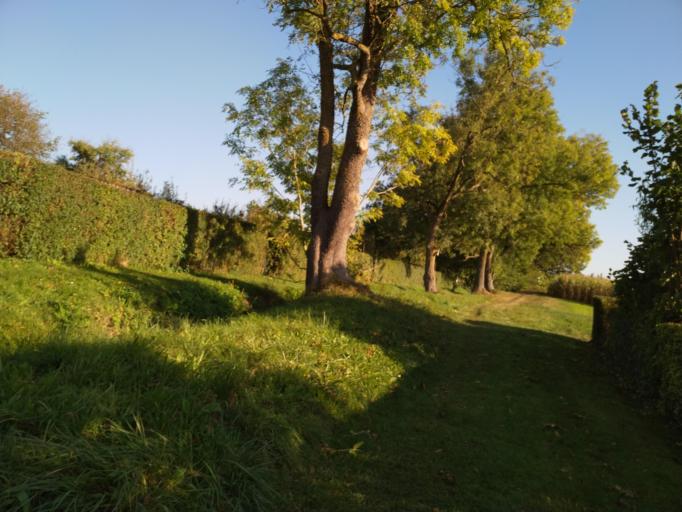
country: DE
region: Bavaria
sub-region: Swabia
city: Guenzburg
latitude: 48.4466
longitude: 10.2959
